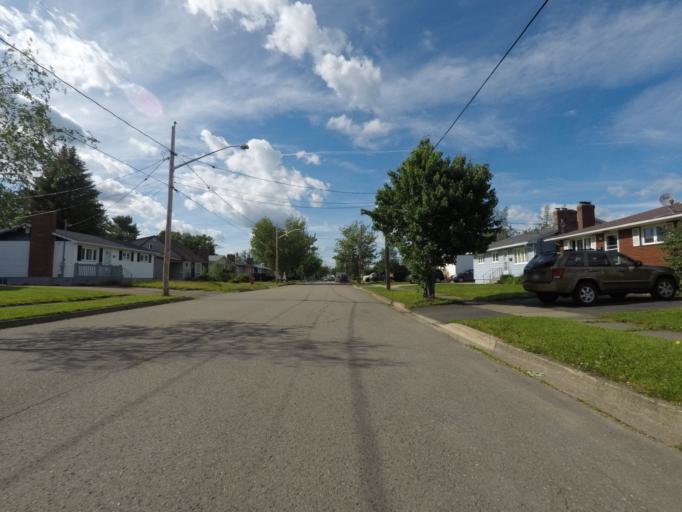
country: CA
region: New Brunswick
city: Moncton
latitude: 46.1013
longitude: -64.8236
